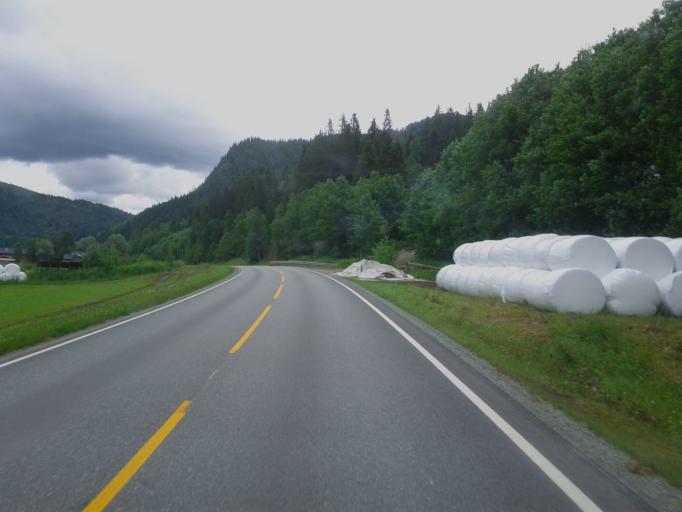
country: NO
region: Sor-Trondelag
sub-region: Midtre Gauldal
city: Storen
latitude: 62.9518
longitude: 10.5950
